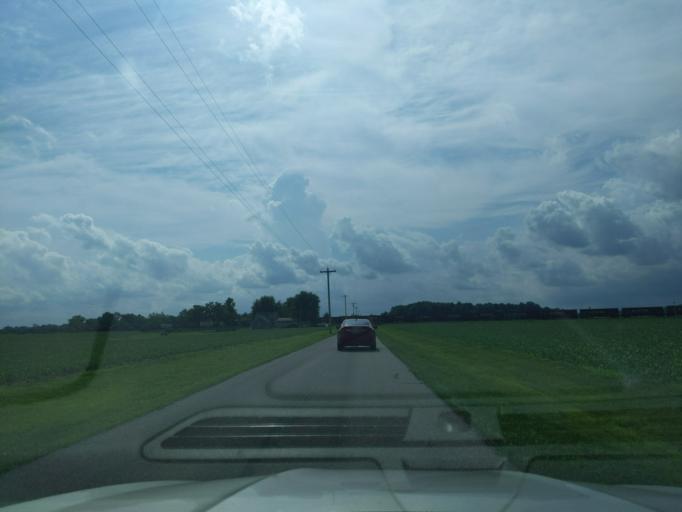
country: US
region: Indiana
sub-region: Ripley County
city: Osgood
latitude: 39.1183
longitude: -85.2997
